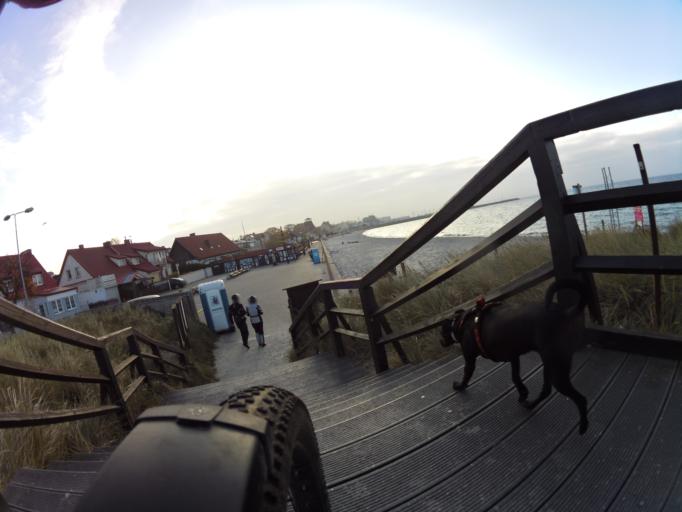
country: PL
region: Pomeranian Voivodeship
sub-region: Powiat pucki
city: Hel
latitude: 54.6076
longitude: 18.7990
